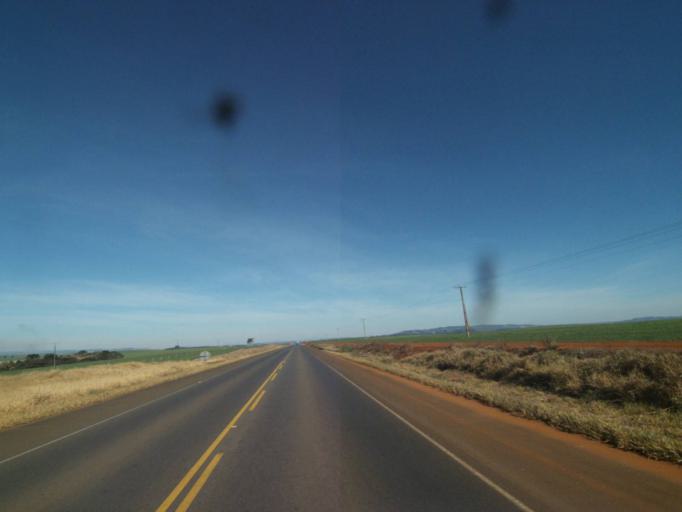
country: BR
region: Parana
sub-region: Tibagi
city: Tibagi
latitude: -24.4423
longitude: -50.4232
